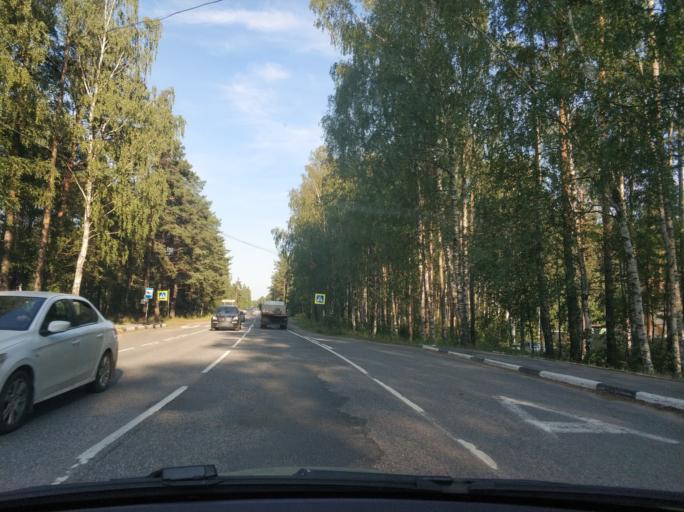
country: RU
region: Leningrad
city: Borisova Griva
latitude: 60.0929
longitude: 30.9846
